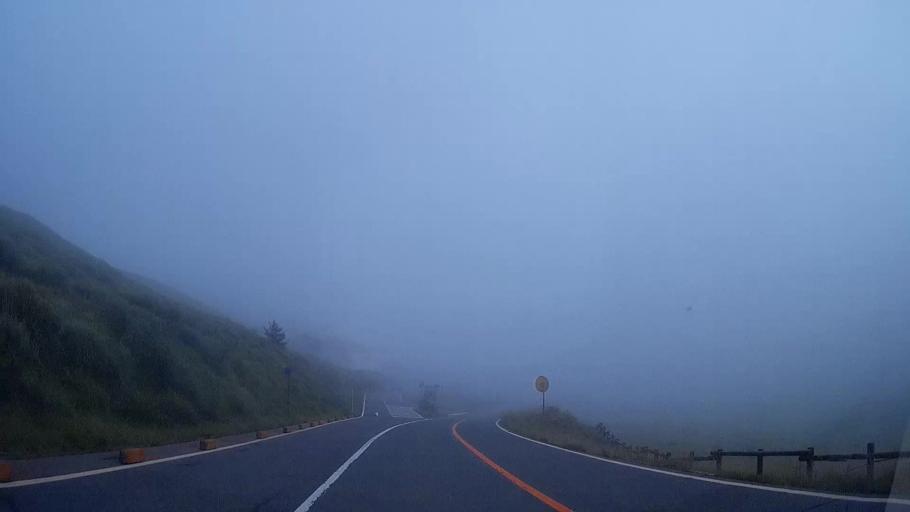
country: JP
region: Kumamoto
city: Aso
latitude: 32.8843
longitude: 131.0507
